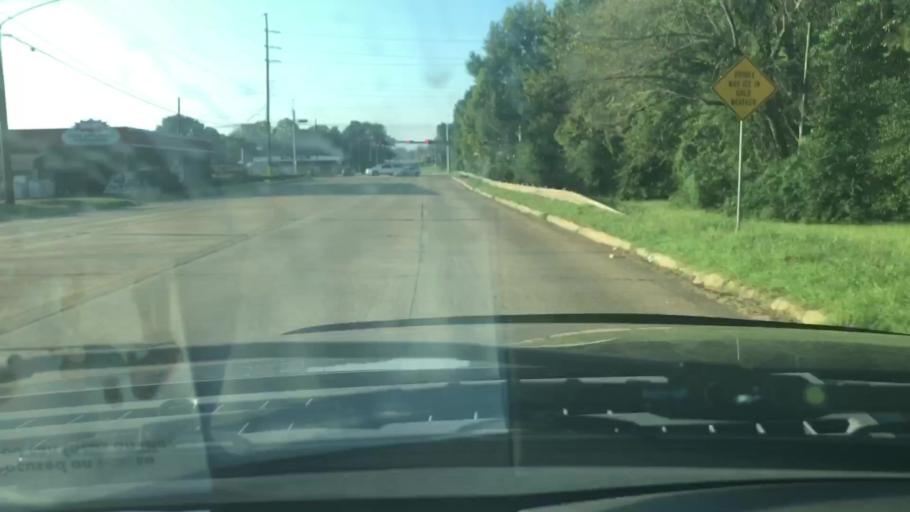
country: US
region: Texas
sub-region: Bowie County
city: Wake Village
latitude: 33.4221
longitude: -94.0803
